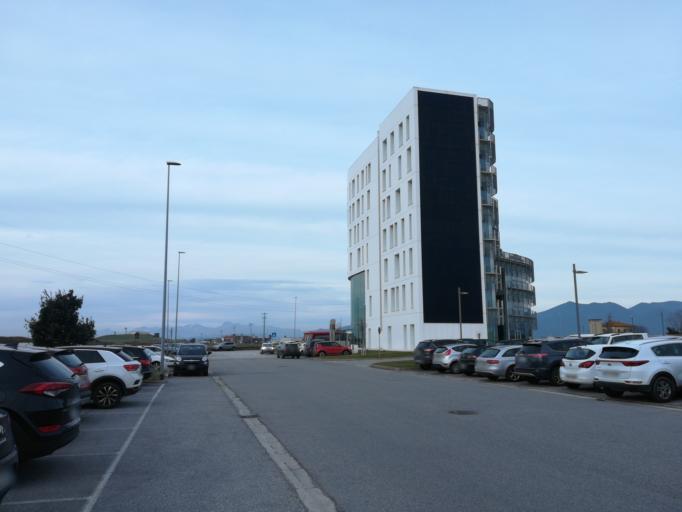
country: IT
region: Tuscany
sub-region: Provincia di Livorno
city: Vicarello
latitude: 43.6582
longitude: 10.4374
